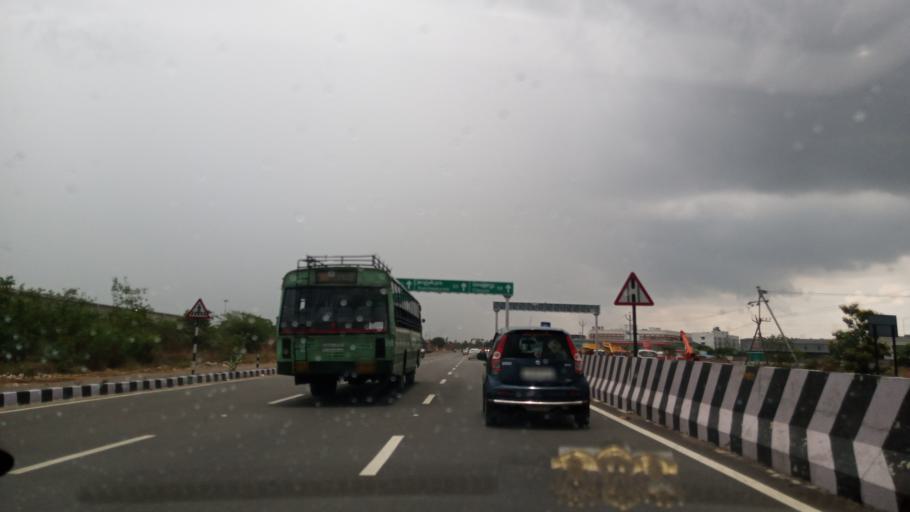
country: IN
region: Tamil Nadu
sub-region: Kancheepuram
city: Madambakkam
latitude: 12.8488
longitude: 79.9396
